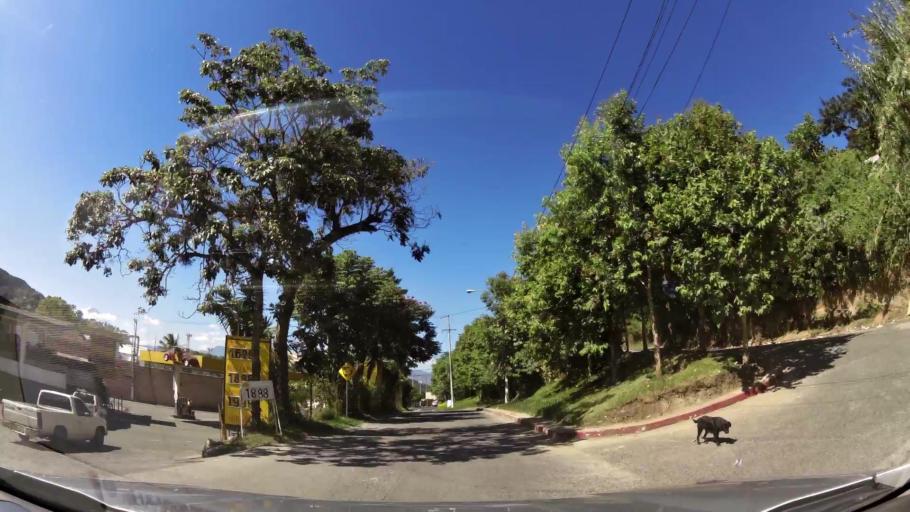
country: GT
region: Guatemala
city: Villa Canales
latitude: 14.4866
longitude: -90.5335
